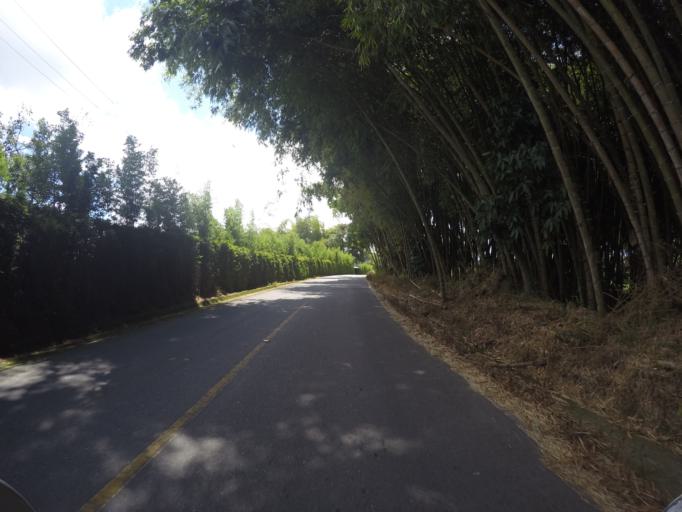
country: CO
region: Quindio
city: Filandia
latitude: 4.6397
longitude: -75.6860
